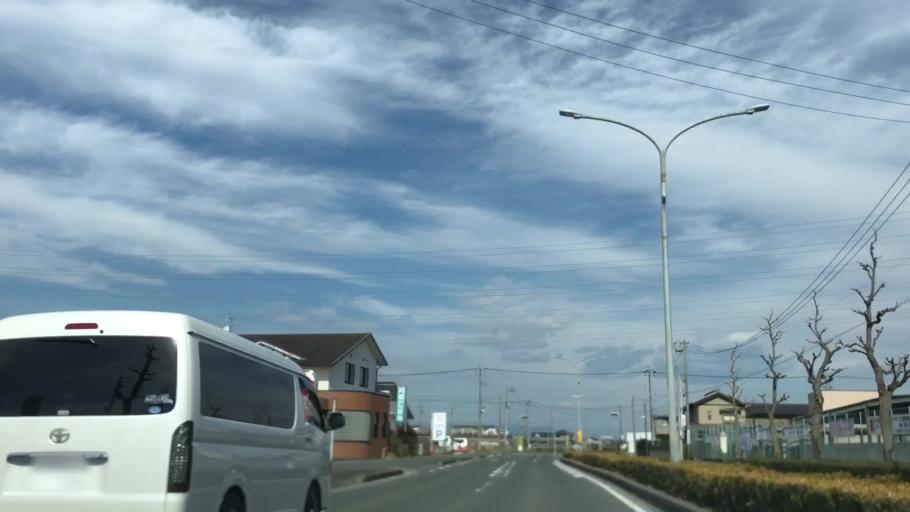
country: JP
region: Shizuoka
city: Hamamatsu
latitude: 34.7329
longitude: 137.6595
